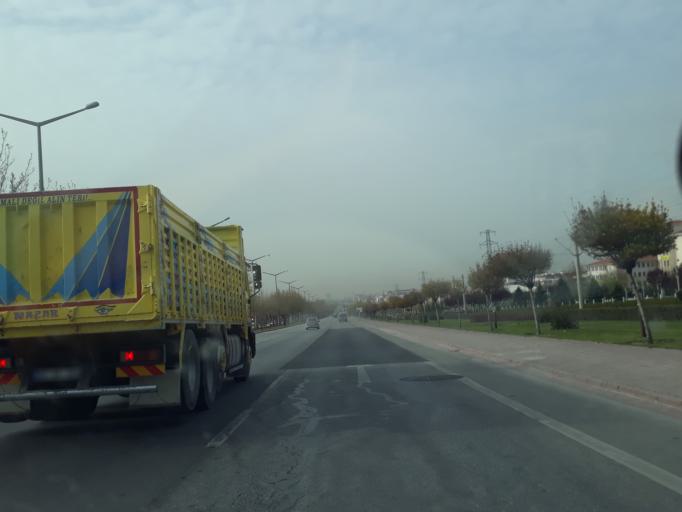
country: TR
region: Konya
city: Asagipinarbasi
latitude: 37.9856
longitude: 32.5176
